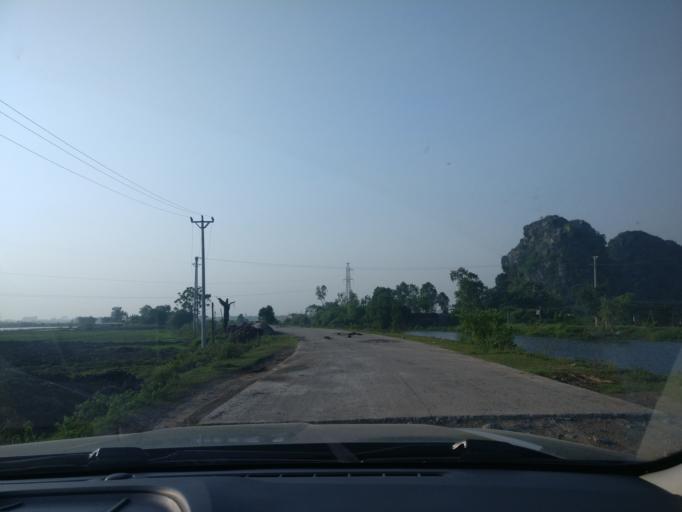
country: VN
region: Ninh Binh
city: Thanh Pho Ninh Binh
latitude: 20.2341
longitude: 105.9428
